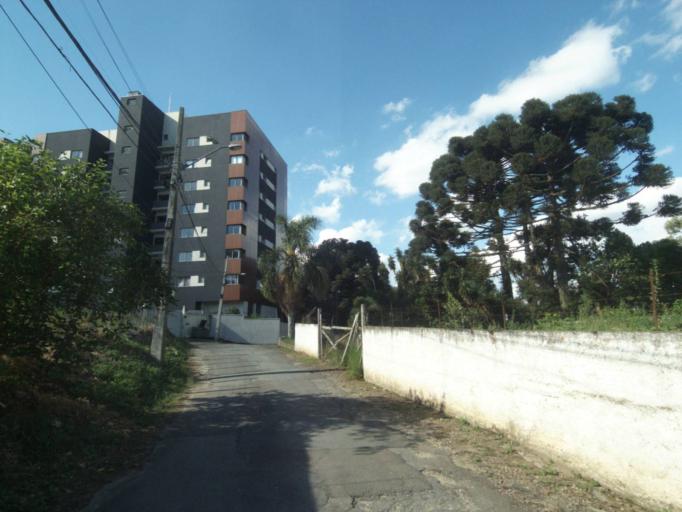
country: BR
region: Parana
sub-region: Curitiba
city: Curitiba
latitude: -25.4420
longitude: -49.3204
